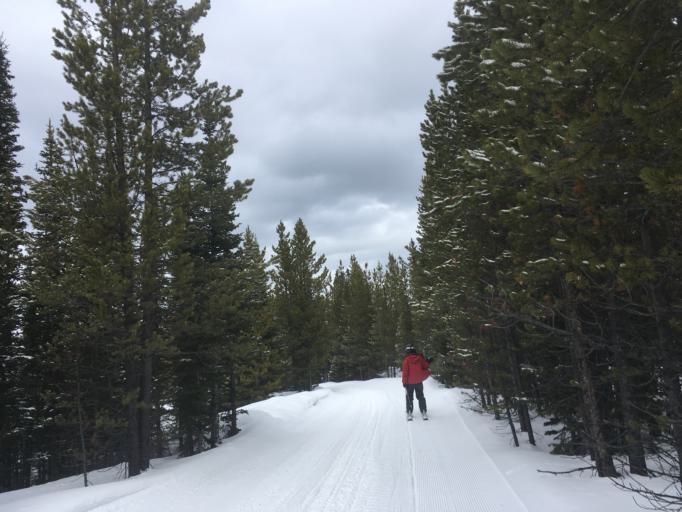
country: US
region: Montana
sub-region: Meagher County
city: White Sulphur Springs
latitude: 46.8494
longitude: -110.7021
